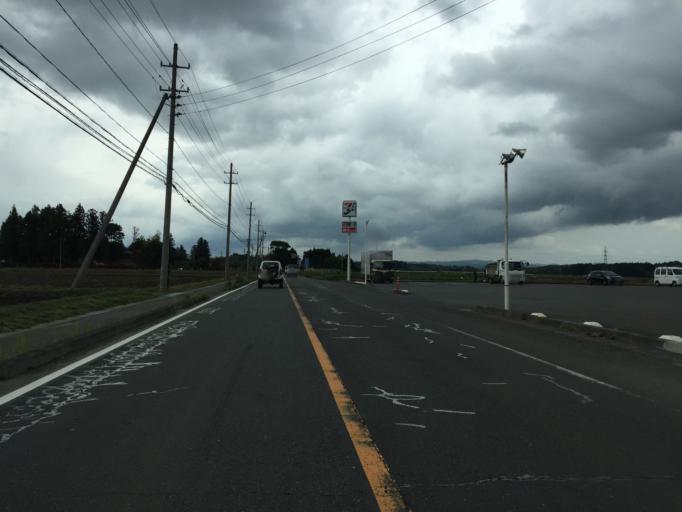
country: JP
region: Fukushima
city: Sukagawa
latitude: 37.1947
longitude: 140.3557
